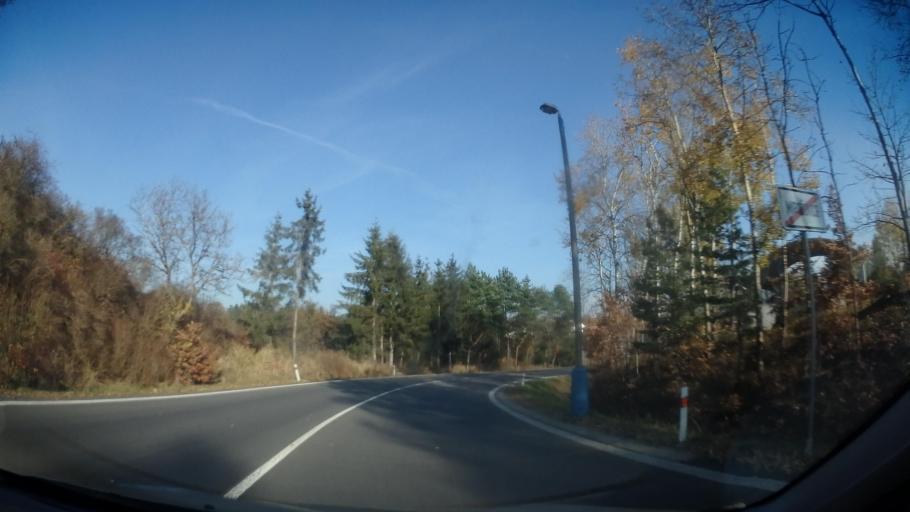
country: CZ
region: Central Bohemia
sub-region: Okres Praha-Vychod
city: Mnichovice
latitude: 49.9104
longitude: 14.7085
